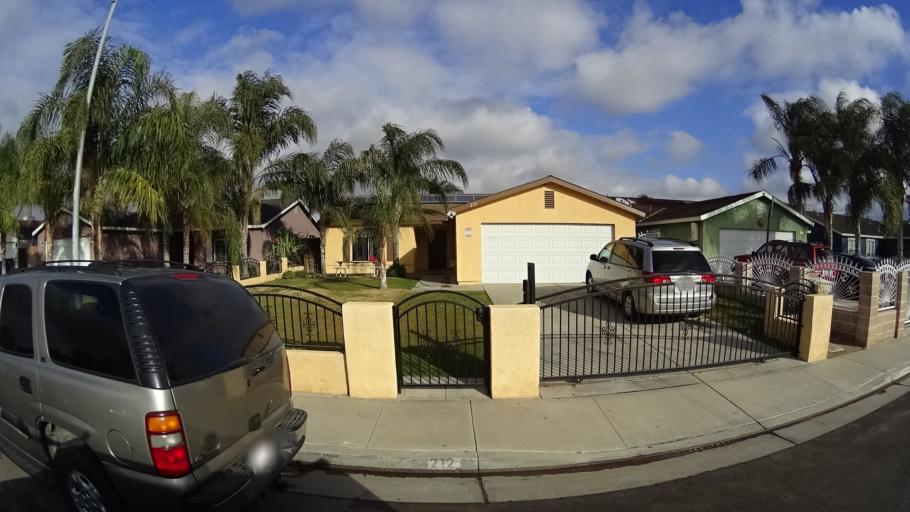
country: US
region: California
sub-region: Kern County
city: Greenfield
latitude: 35.2926
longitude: -119.0051
